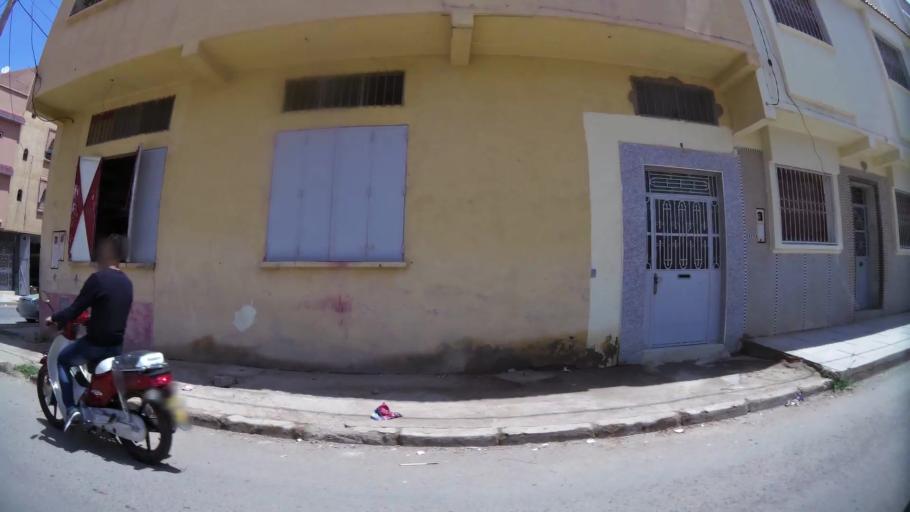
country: MA
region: Oriental
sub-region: Oujda-Angad
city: Oujda
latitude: 34.6887
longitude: -1.8929
